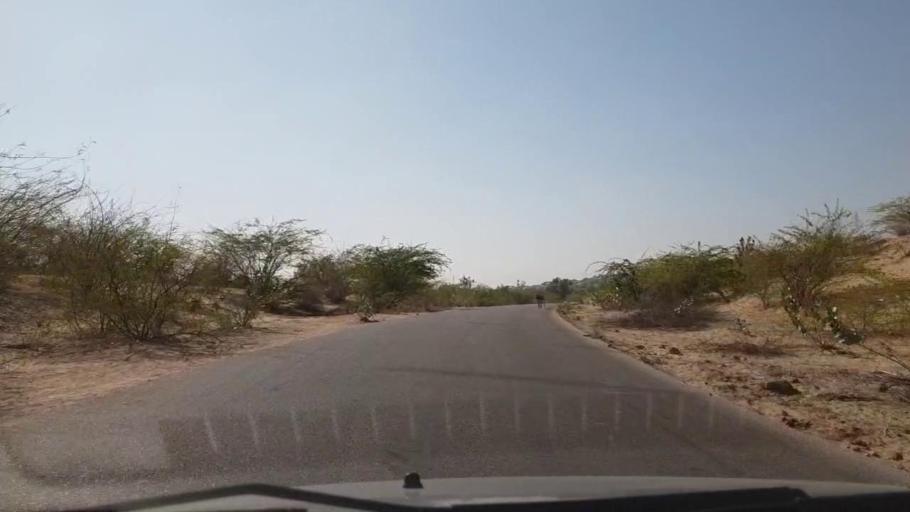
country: PK
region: Sindh
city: Mithi
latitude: 24.5898
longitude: 69.7119
